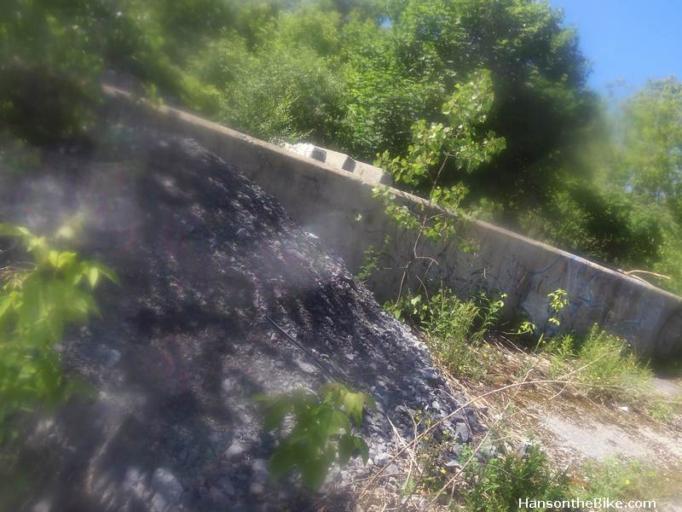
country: CA
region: Ontario
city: Kingston
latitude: 44.2536
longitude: -76.4862
